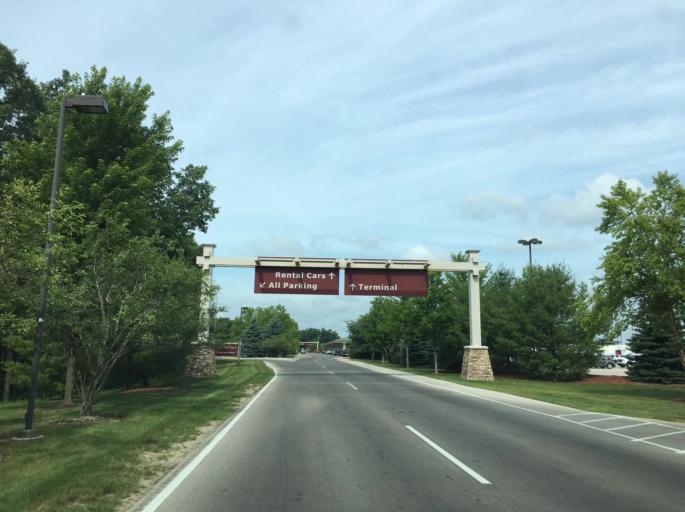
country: US
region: Michigan
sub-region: Grand Traverse County
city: Traverse City
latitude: 44.7363
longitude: -85.5761
